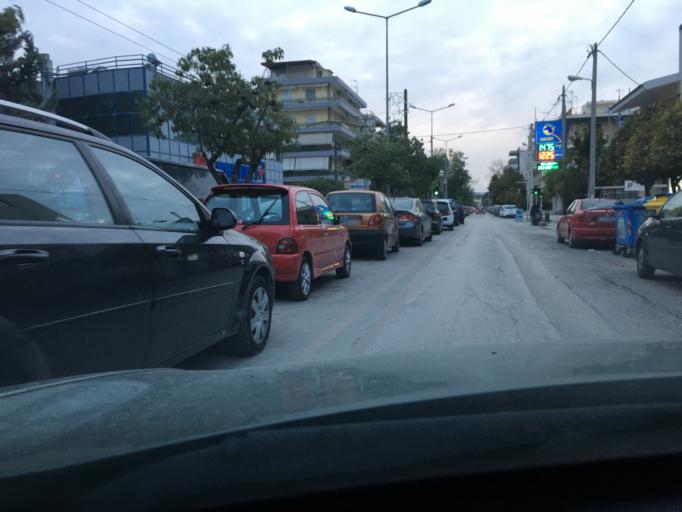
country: GR
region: Attica
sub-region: Nomarchia Athinas
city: Khalandrion
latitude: 38.0227
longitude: 23.7951
